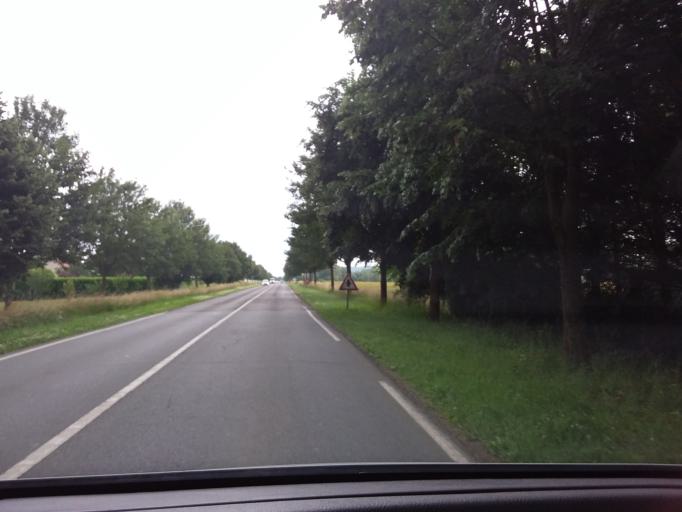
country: FR
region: Picardie
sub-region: Departement de l'Aisne
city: Bucy-le-Long
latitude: 49.3868
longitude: 3.3960
